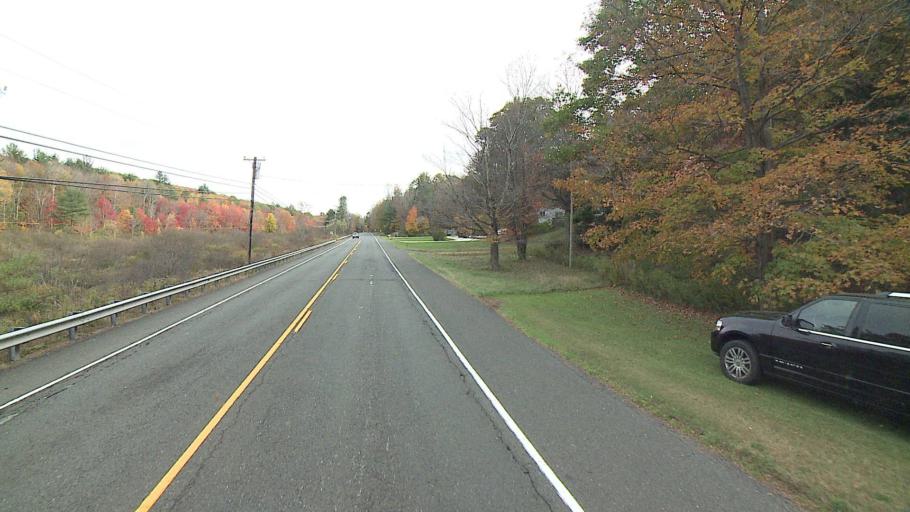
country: US
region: Connecticut
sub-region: Litchfield County
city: Winchester Center
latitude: 41.9579
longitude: -73.1184
